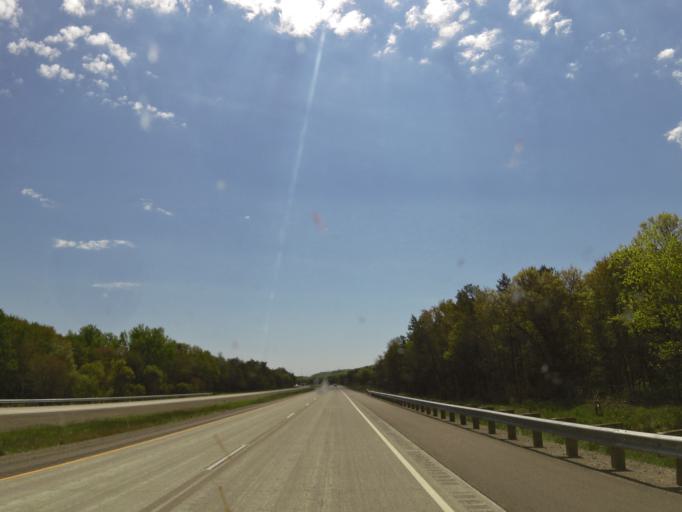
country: US
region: Wisconsin
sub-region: Jackson County
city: Black River Falls
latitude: 44.3584
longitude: -90.9579
